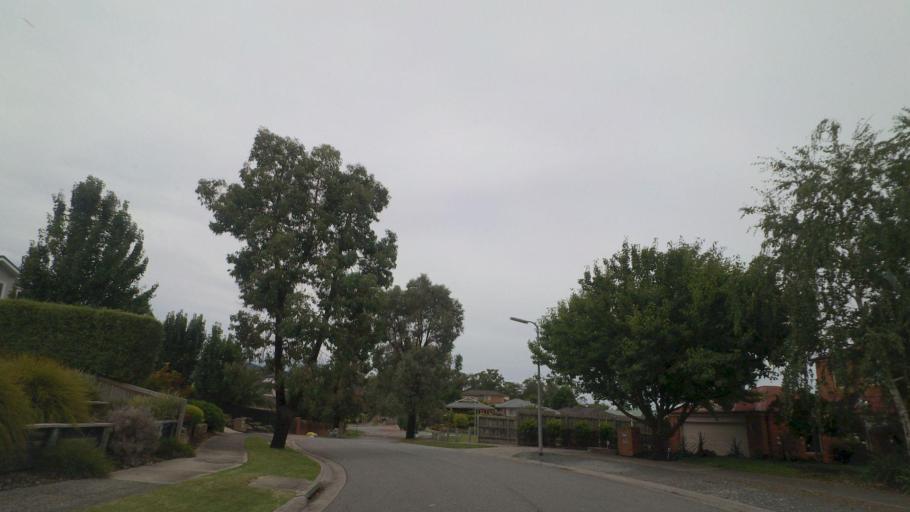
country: AU
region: Victoria
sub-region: Yarra Ranges
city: Kilsyth
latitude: -37.7808
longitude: 145.3373
